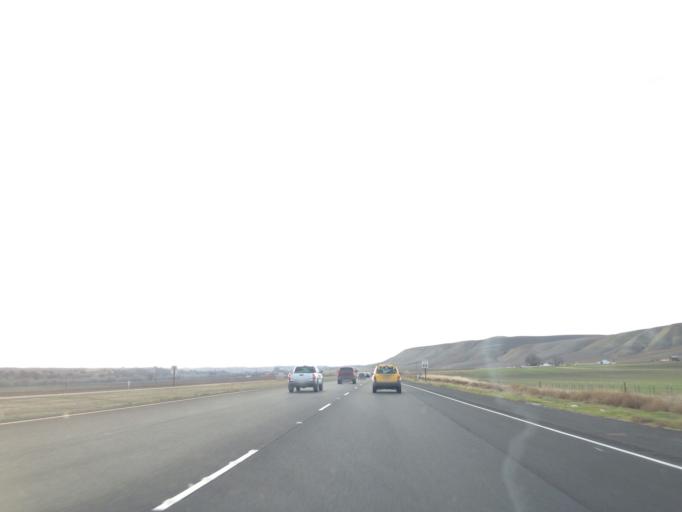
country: US
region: California
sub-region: San Luis Obispo County
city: Shandon
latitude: 35.6616
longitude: -120.4208
